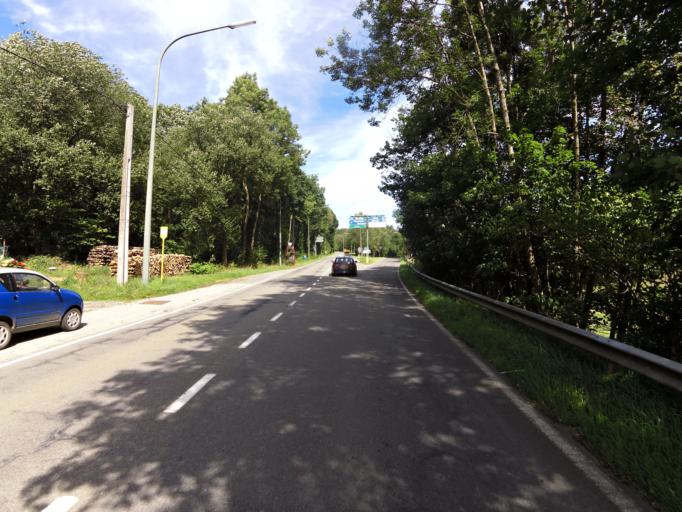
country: BE
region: Wallonia
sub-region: Province du Luxembourg
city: Saint-Hubert
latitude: 50.0319
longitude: 5.3834
